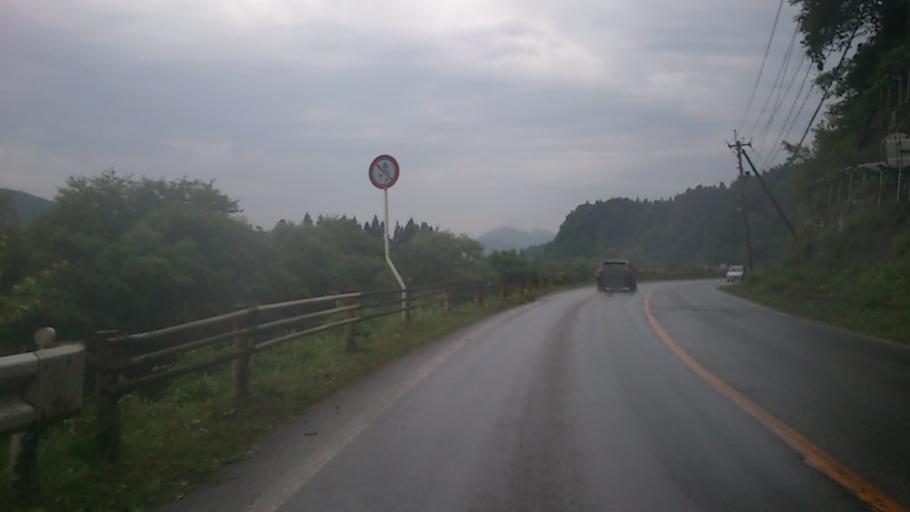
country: JP
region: Akita
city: Takanosu
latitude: 40.2387
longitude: 140.2432
